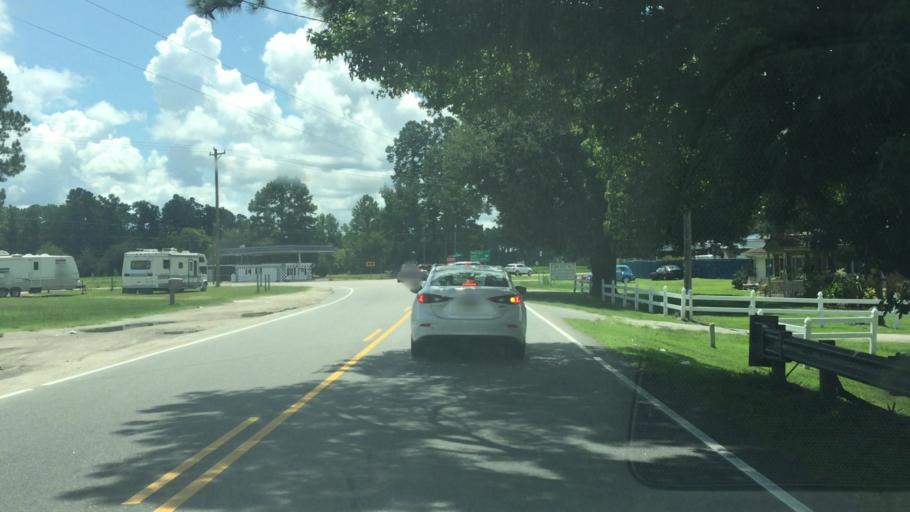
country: US
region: North Carolina
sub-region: Columbus County
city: Tabor City
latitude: 34.1619
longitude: -78.8464
